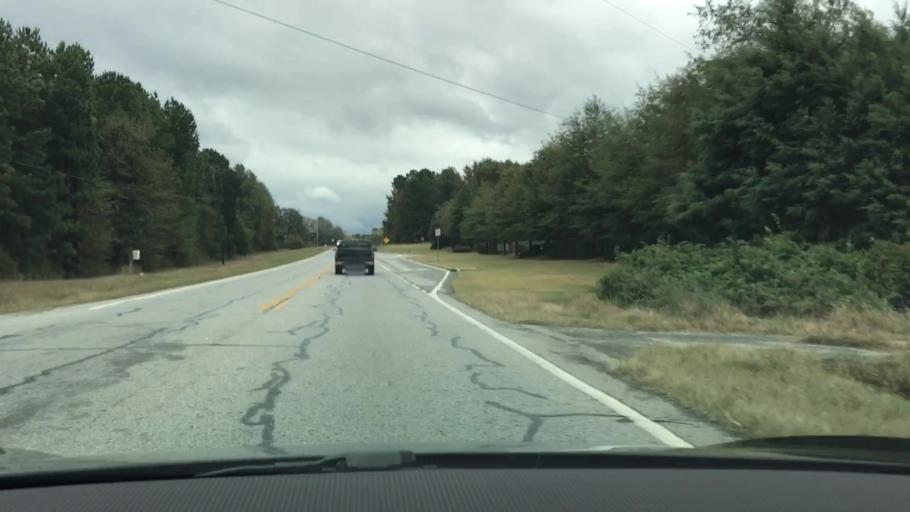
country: US
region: Georgia
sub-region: Oconee County
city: Watkinsville
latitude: 33.8467
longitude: -83.3918
